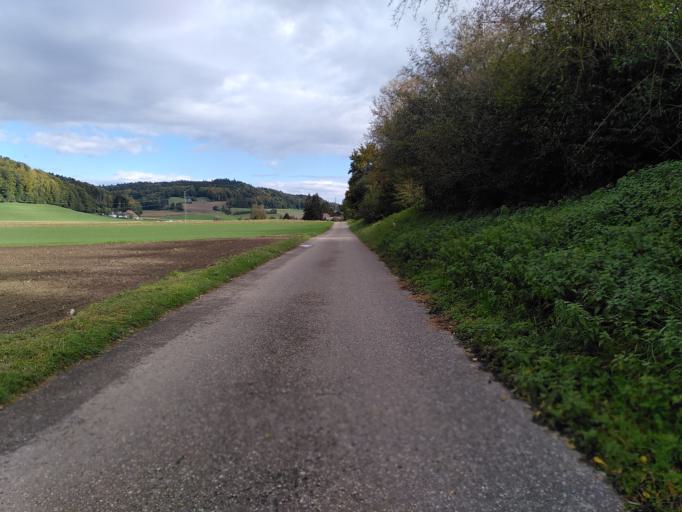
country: CH
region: Bern
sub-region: Emmental District
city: Wynigen
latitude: 47.1208
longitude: 7.6713
